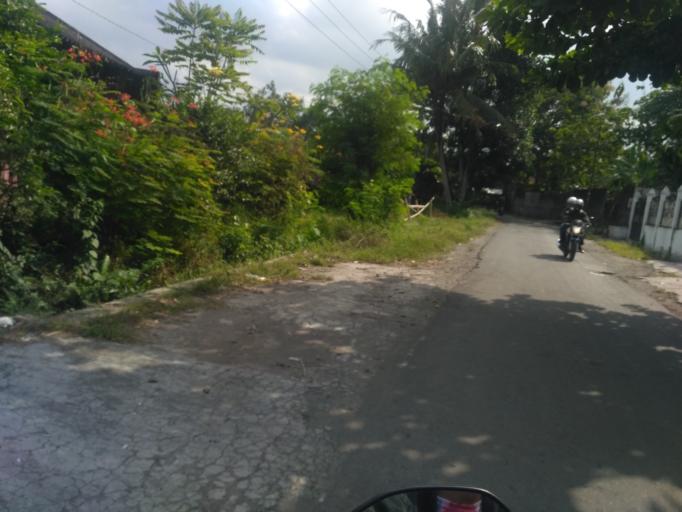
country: ID
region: Daerah Istimewa Yogyakarta
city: Yogyakarta
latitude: -7.7621
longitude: 110.3589
